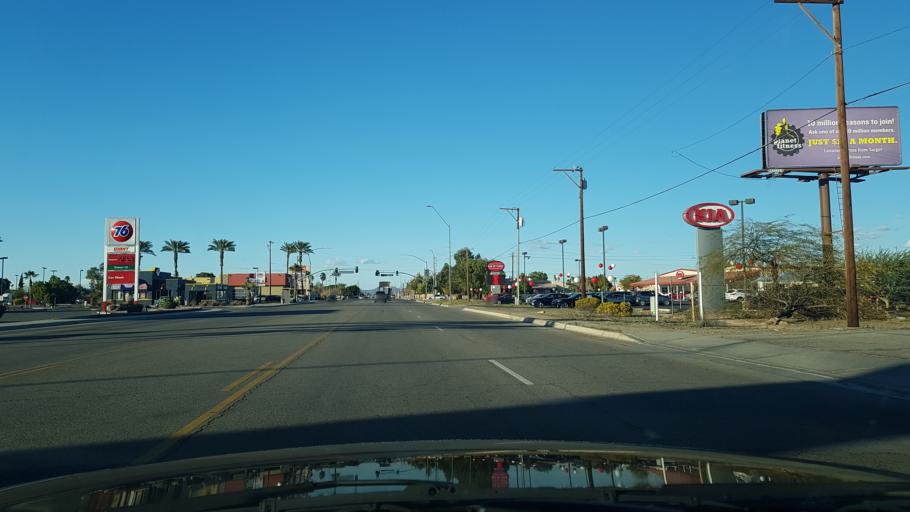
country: US
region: Arizona
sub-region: Yuma County
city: Yuma
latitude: 32.6752
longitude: -114.5988
